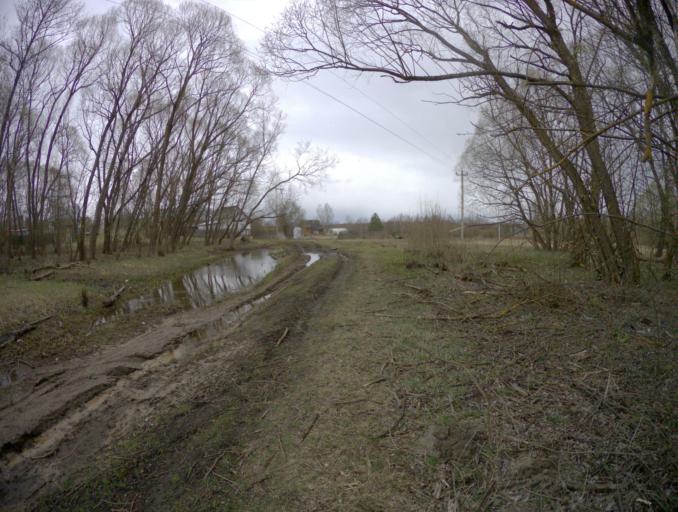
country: RU
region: Vladimir
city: Sudogda
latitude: 56.0135
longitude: 40.8050
